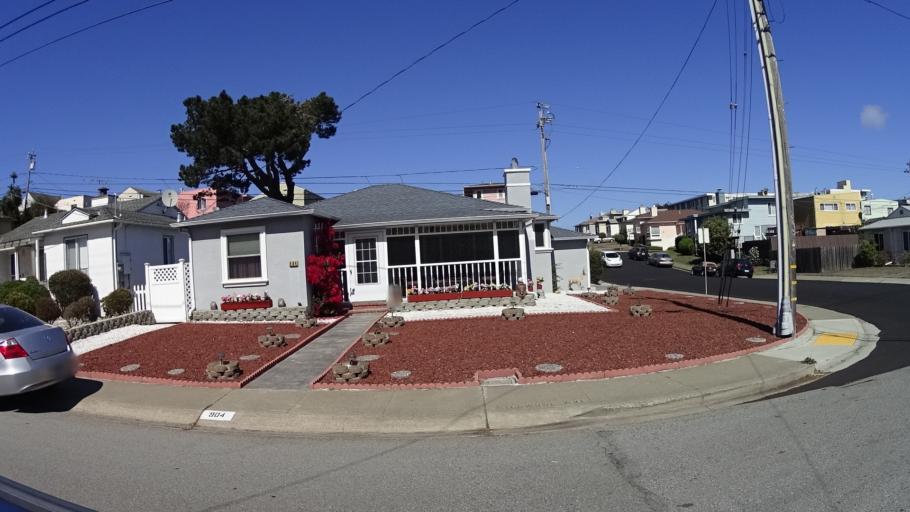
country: US
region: California
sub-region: San Mateo County
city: Broadmoor
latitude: 37.6959
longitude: -122.4868
